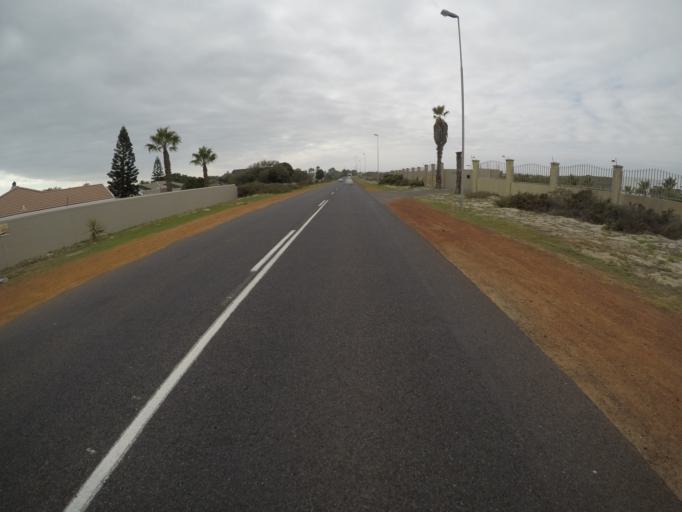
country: ZA
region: Western Cape
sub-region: City of Cape Town
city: Atlantis
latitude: -33.7006
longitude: 18.4452
